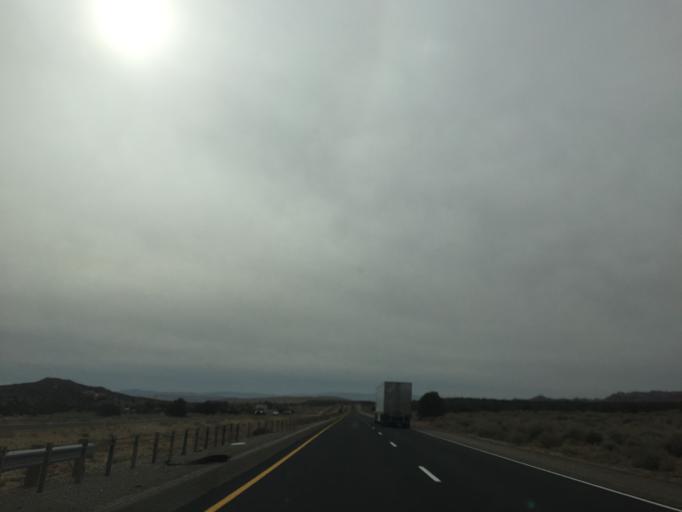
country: US
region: Utah
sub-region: Washington County
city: Toquerville
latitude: 37.2692
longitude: -113.3210
